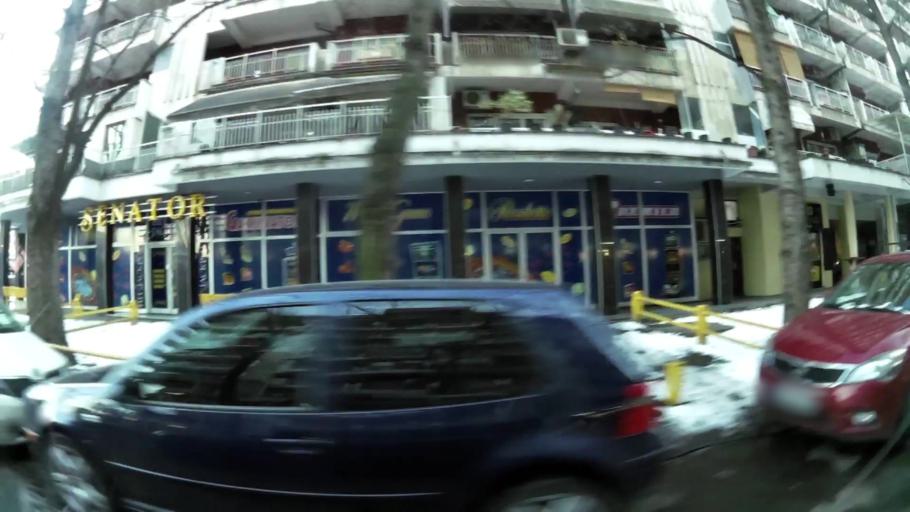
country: MK
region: Karpos
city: Skopje
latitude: 41.9939
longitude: 21.4154
